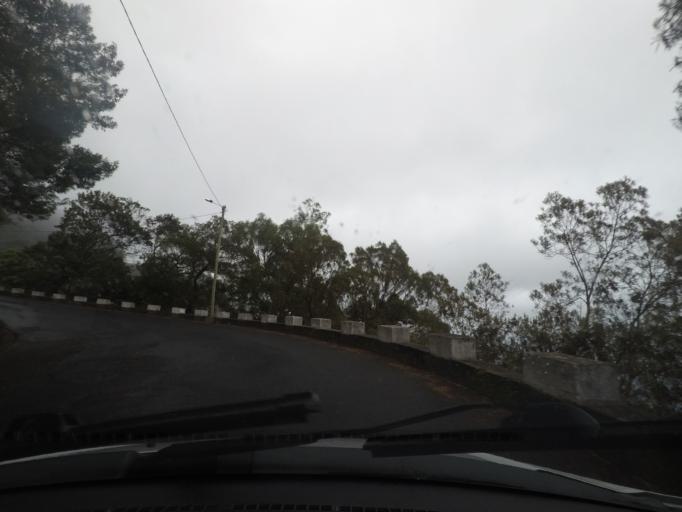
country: PT
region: Madeira
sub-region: Santana
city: Santana
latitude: 32.7862
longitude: -16.8596
